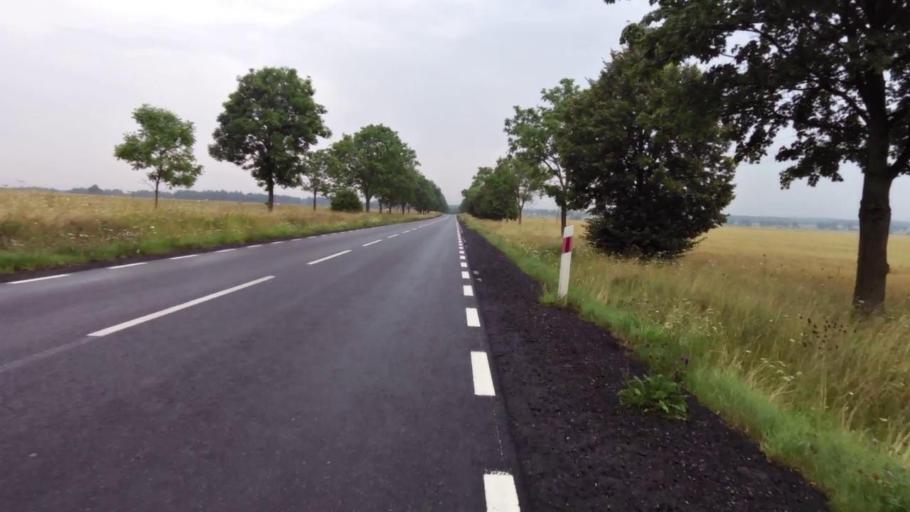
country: PL
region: West Pomeranian Voivodeship
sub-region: Powiat stargardzki
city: Insko
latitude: 53.4566
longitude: 15.5803
